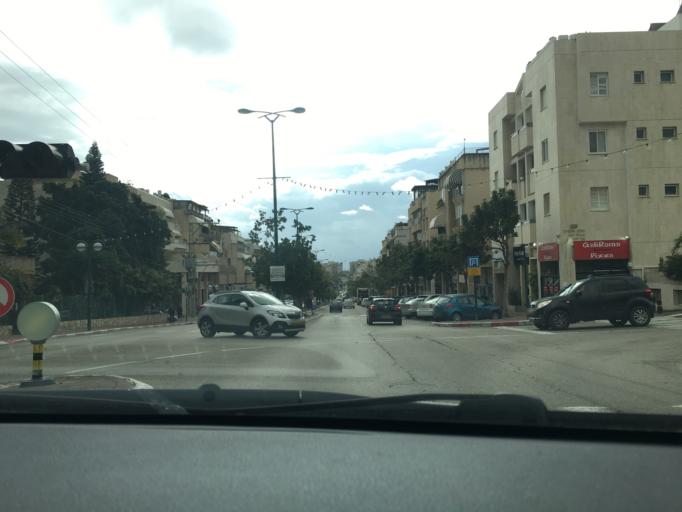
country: IL
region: Tel Aviv
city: Ramat HaSharon
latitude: 32.1426
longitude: 34.8434
